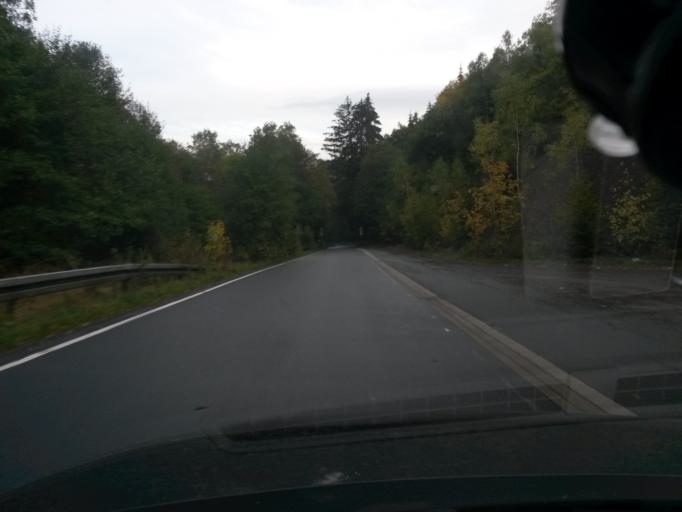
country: DE
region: North Rhine-Westphalia
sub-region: Regierungsbezirk Arnsberg
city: Herscheid
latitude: 51.2162
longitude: 7.7252
